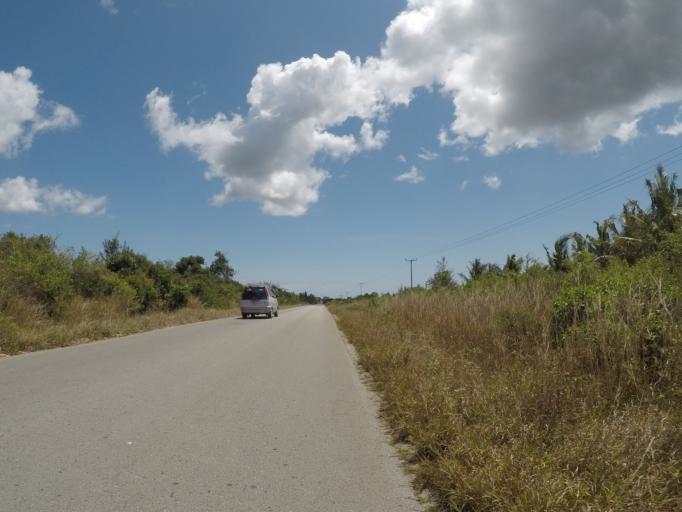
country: TZ
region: Zanzibar Central/South
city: Nganane
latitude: -6.2766
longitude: 39.4846
